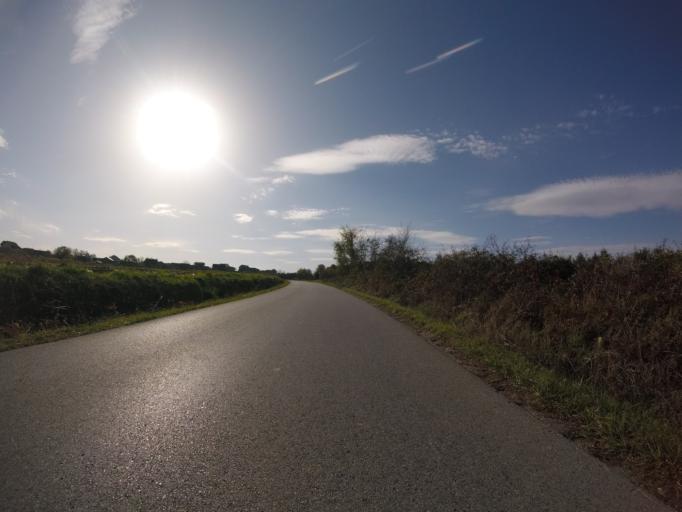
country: HR
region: Zagrebacka
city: Gradici
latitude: 45.6384
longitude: 16.0317
